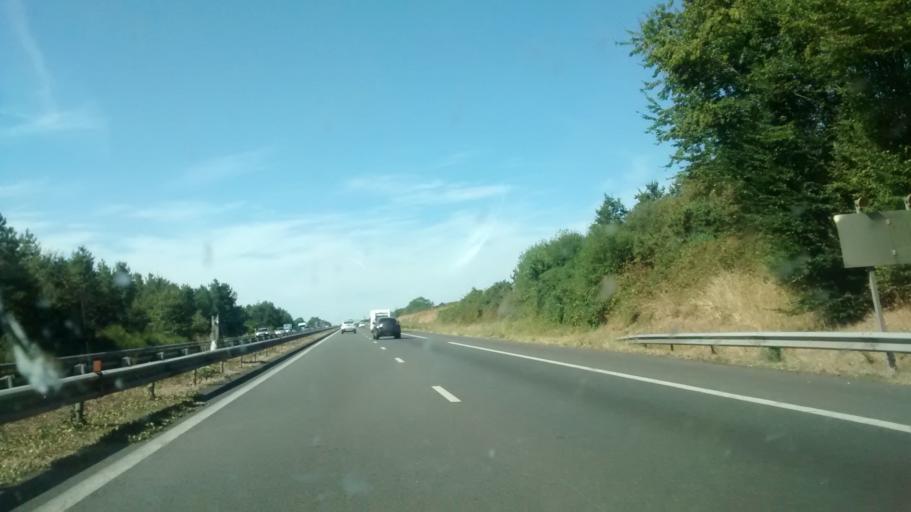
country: FR
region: Pays de la Loire
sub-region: Departement de la Loire-Atlantique
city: Le Bignon
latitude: 47.1190
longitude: -1.4958
